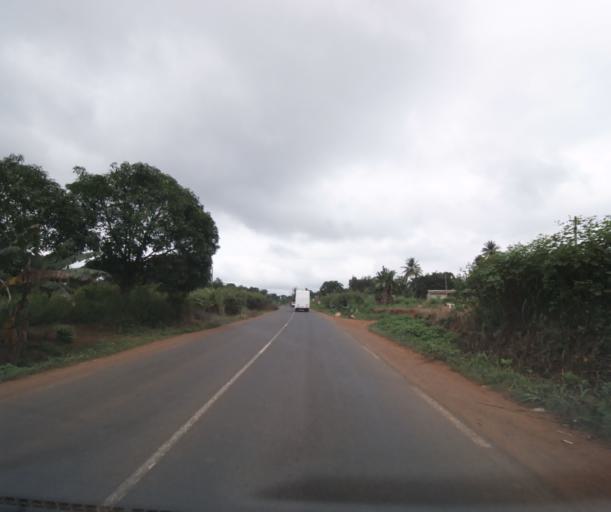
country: CM
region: Centre
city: Mbankomo
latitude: 3.7895
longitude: 11.4343
